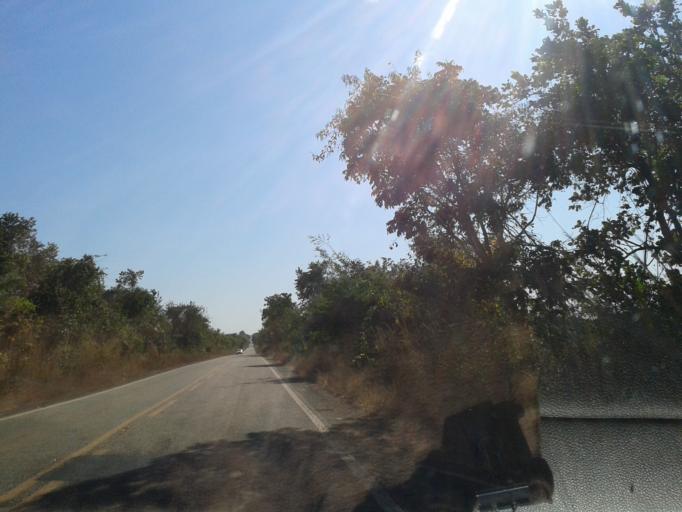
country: BR
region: Goias
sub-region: Mozarlandia
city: Mozarlandia
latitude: -14.6169
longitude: -50.5173
